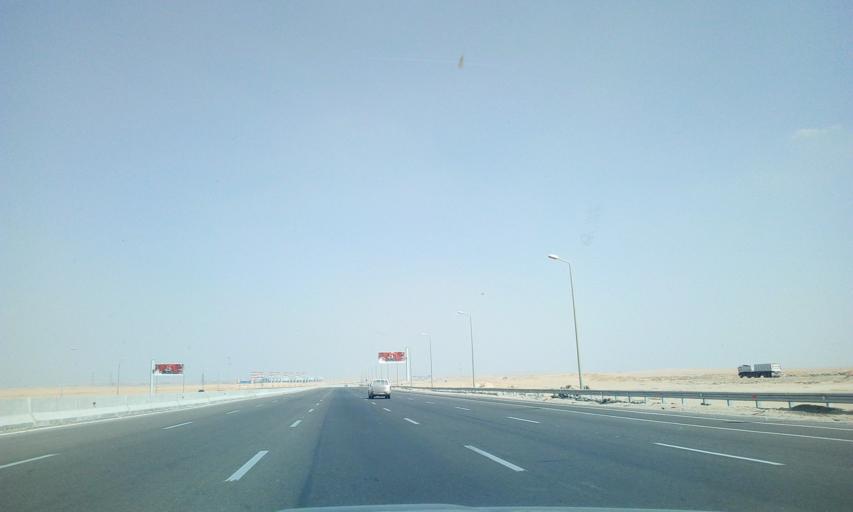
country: EG
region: Muhafazat al Qahirah
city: Halwan
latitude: 29.9058
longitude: 31.7228
